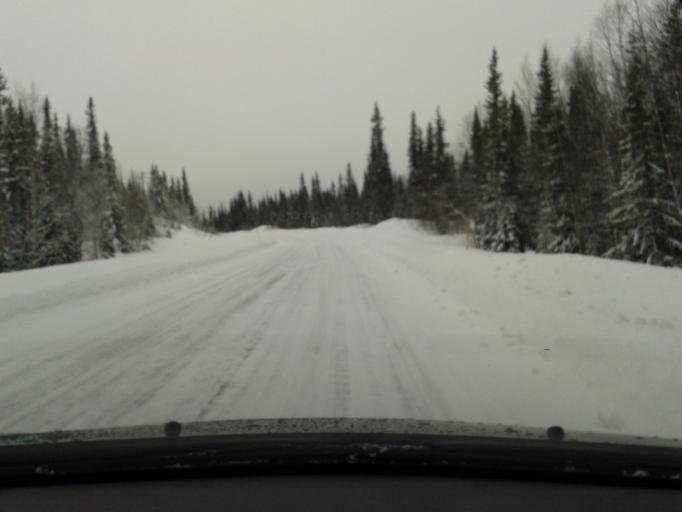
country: SE
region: Vaesterbotten
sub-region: Vilhelmina Kommun
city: Sjoberg
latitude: 65.1597
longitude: 15.8680
